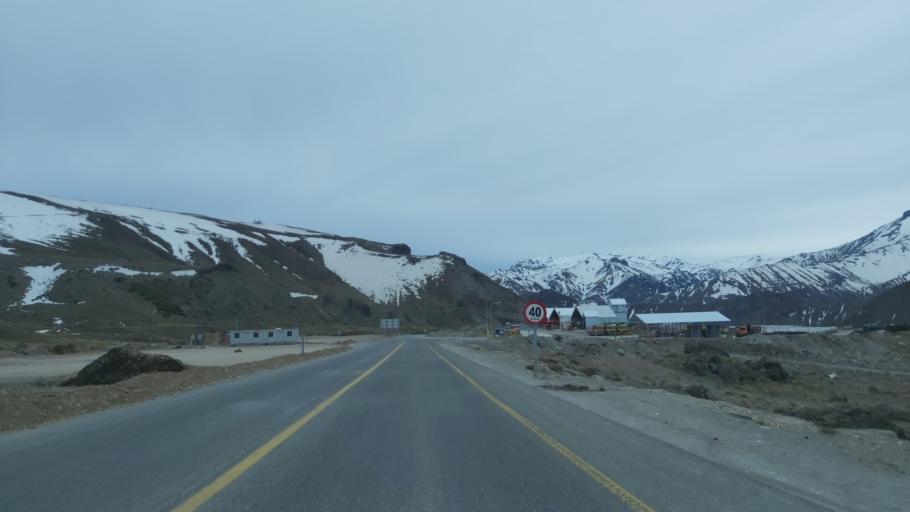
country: CL
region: Maule
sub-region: Provincia de Linares
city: Colbun
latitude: -35.9702
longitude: -70.5685
